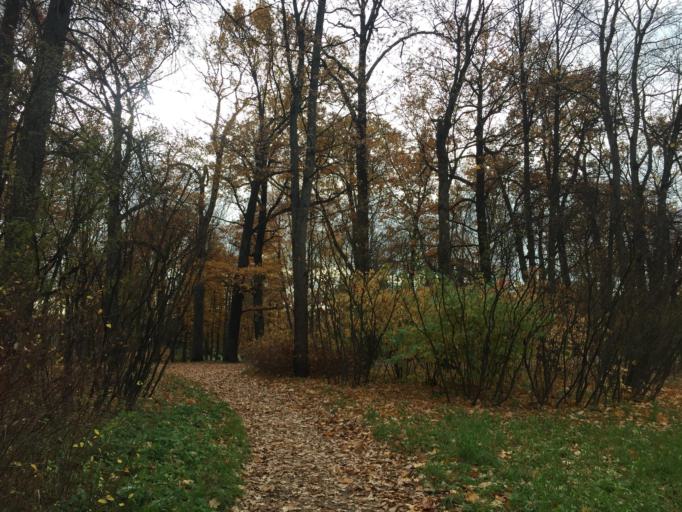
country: RU
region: St.-Petersburg
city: Pushkin
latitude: 59.7118
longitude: 30.3882
